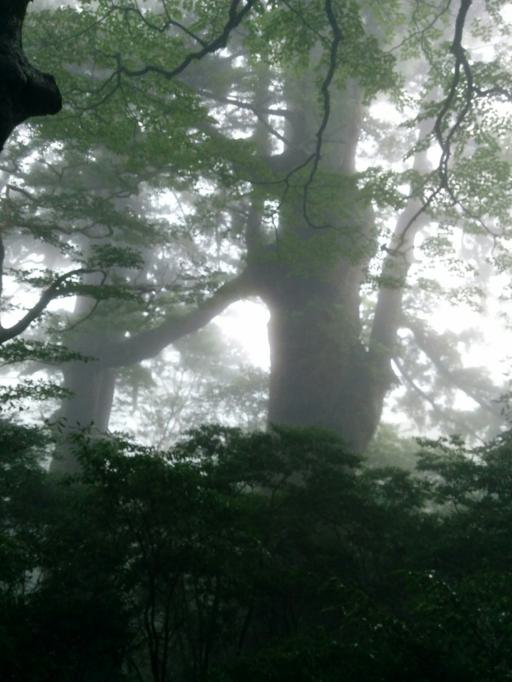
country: JP
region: Kagoshima
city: Nishinoomote
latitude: 30.3600
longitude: 130.5360
